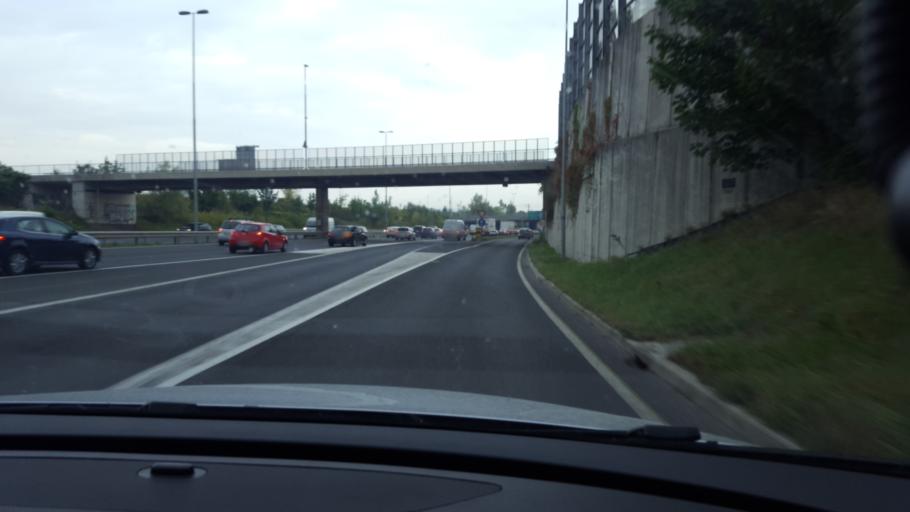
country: SI
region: Dol pri Ljubljani
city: Dol pri Ljubljani
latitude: 46.0563
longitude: 14.5740
